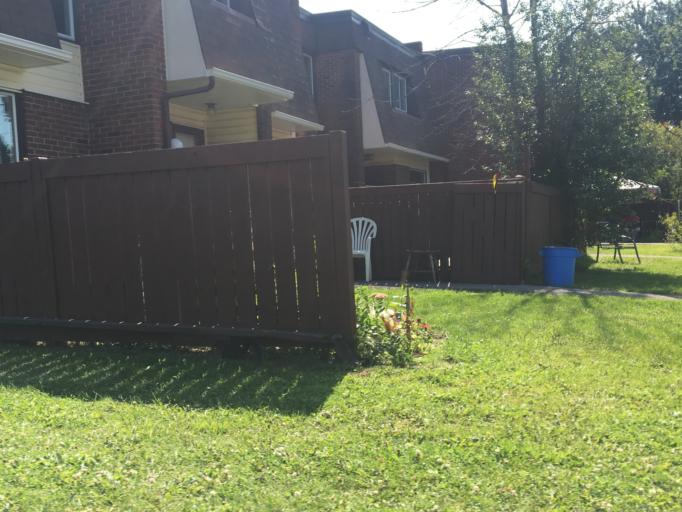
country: CA
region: Ontario
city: Ottawa
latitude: 45.3786
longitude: -75.6407
